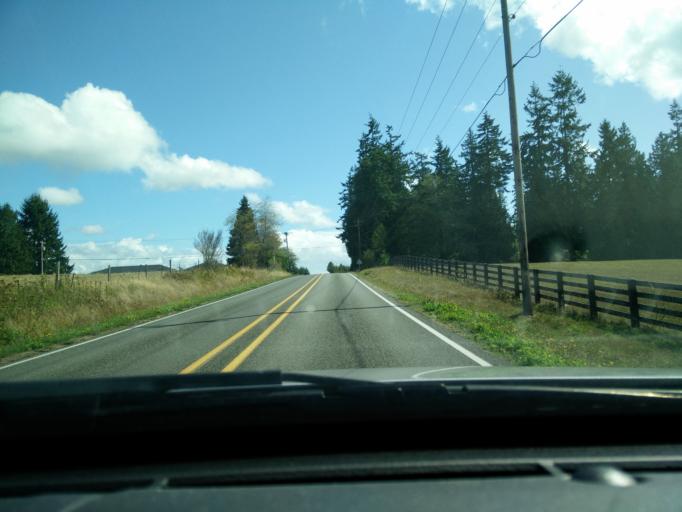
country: US
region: Washington
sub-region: Snohomish County
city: Stanwood
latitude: 48.2685
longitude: -122.3380
